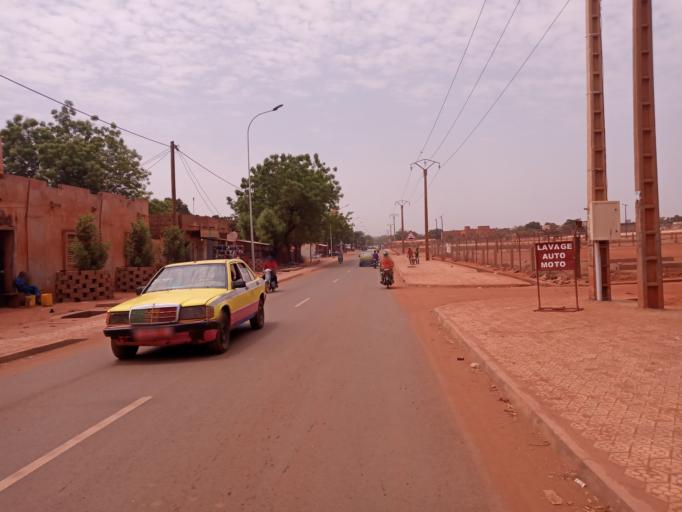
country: ML
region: Bamako
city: Bamako
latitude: 12.5855
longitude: -7.9882
